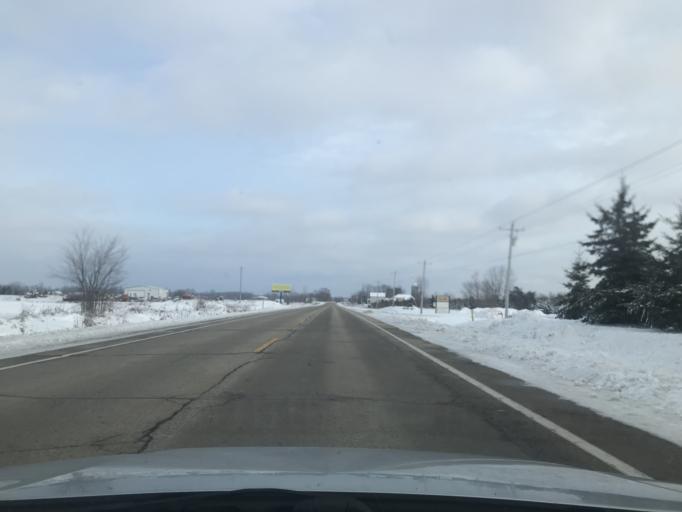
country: US
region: Wisconsin
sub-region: Oconto County
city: Oconto
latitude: 44.8927
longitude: -87.9450
